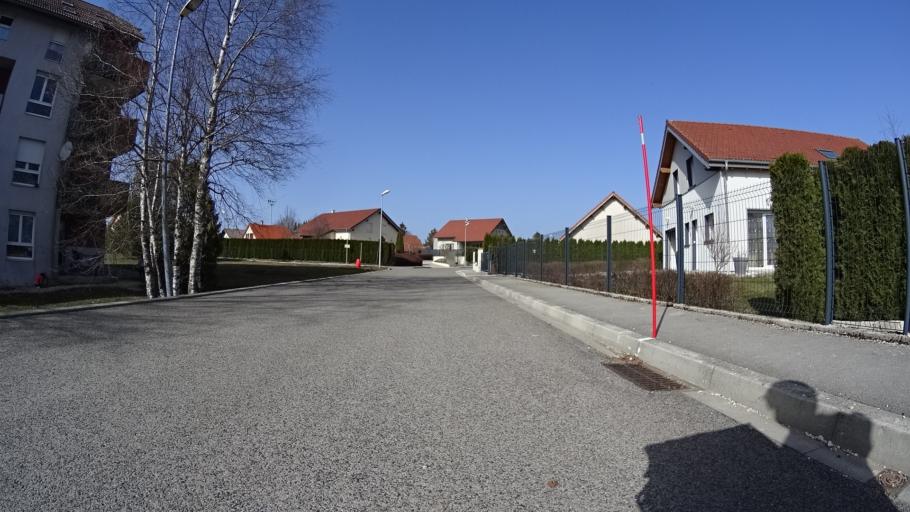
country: FR
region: Franche-Comte
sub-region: Departement du Doubs
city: Frasne
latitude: 46.8514
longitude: 6.1614
